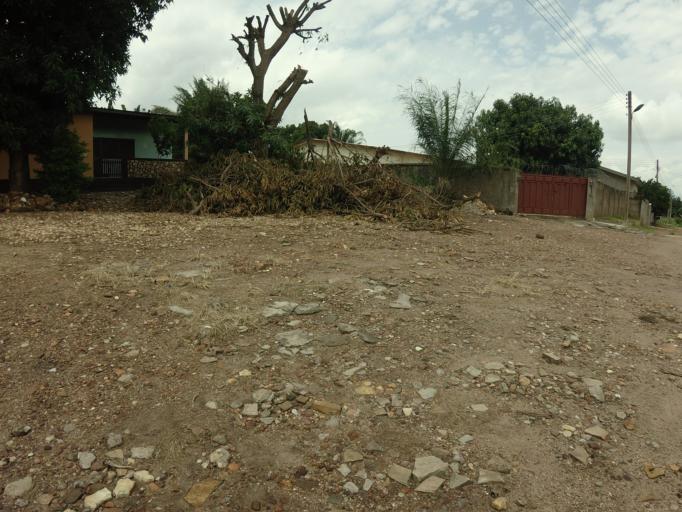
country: GH
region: Volta
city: Ho
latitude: 6.5925
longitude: 0.4725
